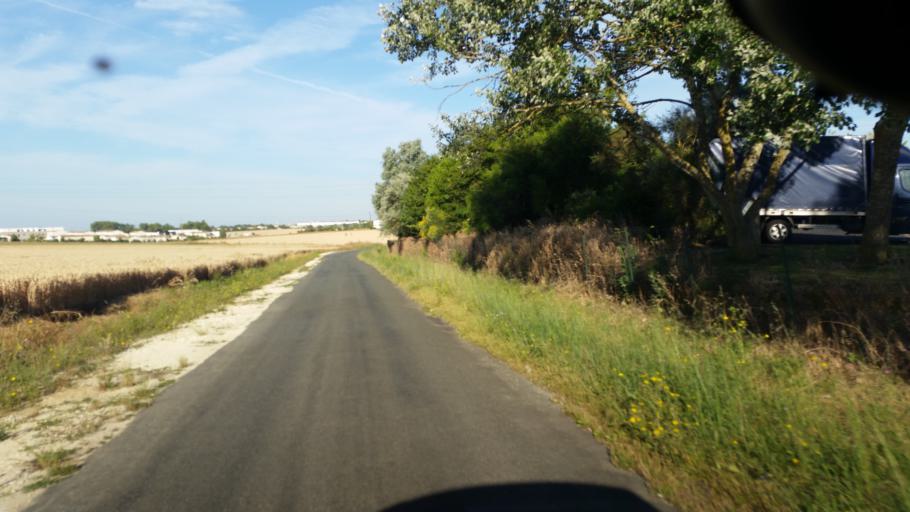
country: FR
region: Poitou-Charentes
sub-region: Departement de la Charente-Maritime
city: Puilboreau
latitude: 46.1762
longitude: -1.1025
